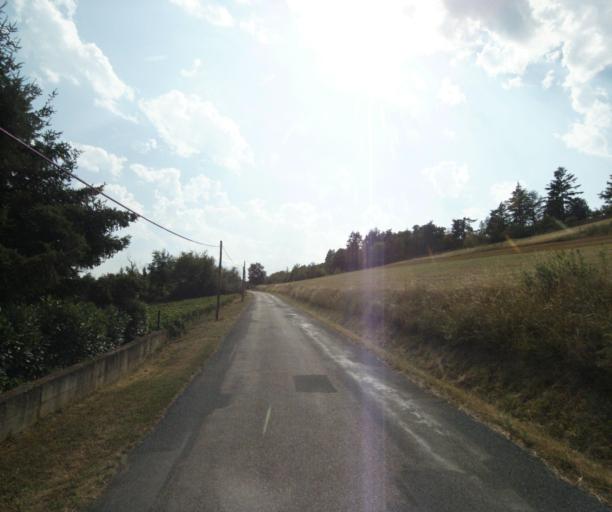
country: FR
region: Rhone-Alpes
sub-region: Departement du Rhone
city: Bully
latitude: 45.8567
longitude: 4.5938
